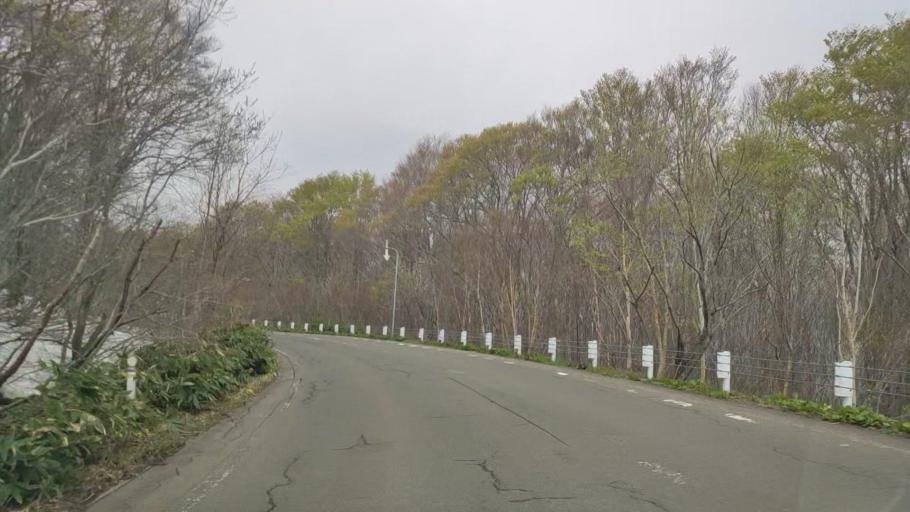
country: JP
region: Aomori
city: Aomori Shi
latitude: 40.6590
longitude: 140.9608
